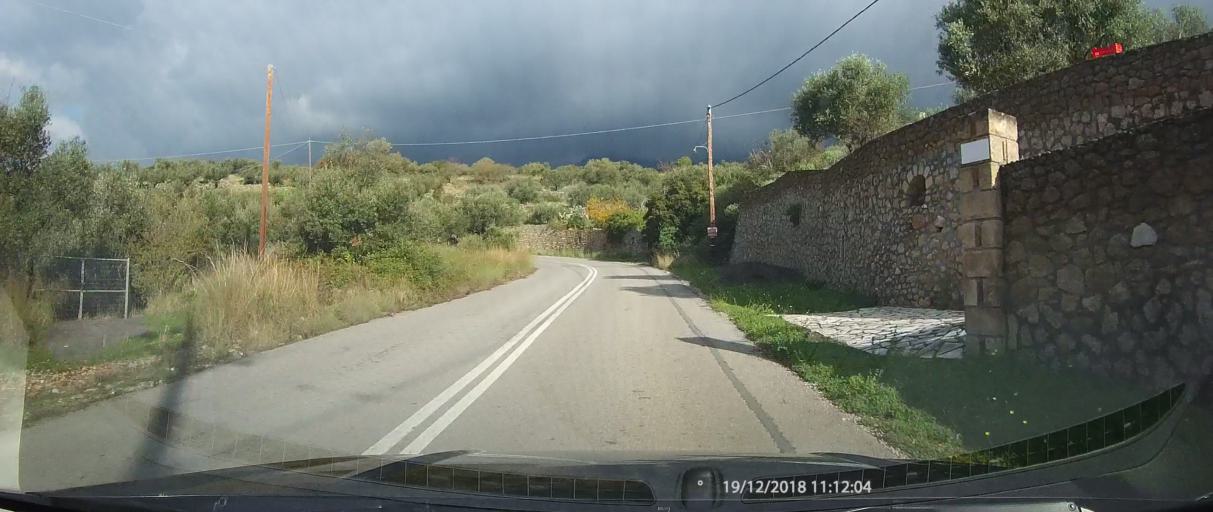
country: GR
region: Peloponnese
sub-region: Nomos Messinias
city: Kardamyli
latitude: 36.8196
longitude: 22.3055
